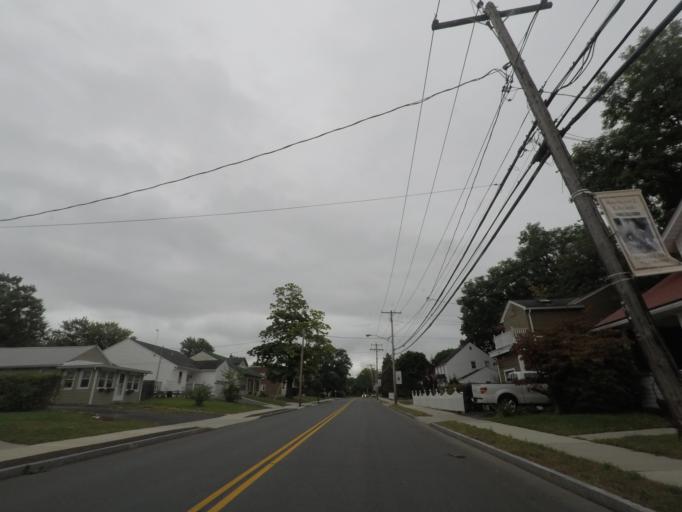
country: US
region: New York
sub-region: Rensselaer County
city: Rensselaer
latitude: 42.6580
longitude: -73.7141
